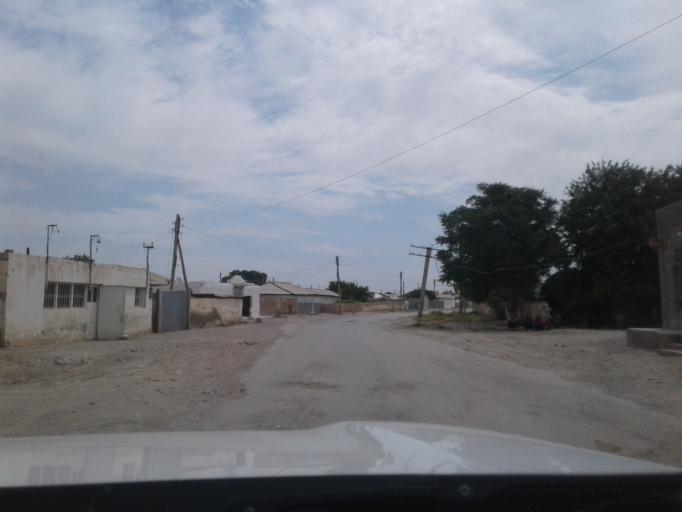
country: TM
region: Balkan
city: Serdar
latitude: 38.9891
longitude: 56.2720
